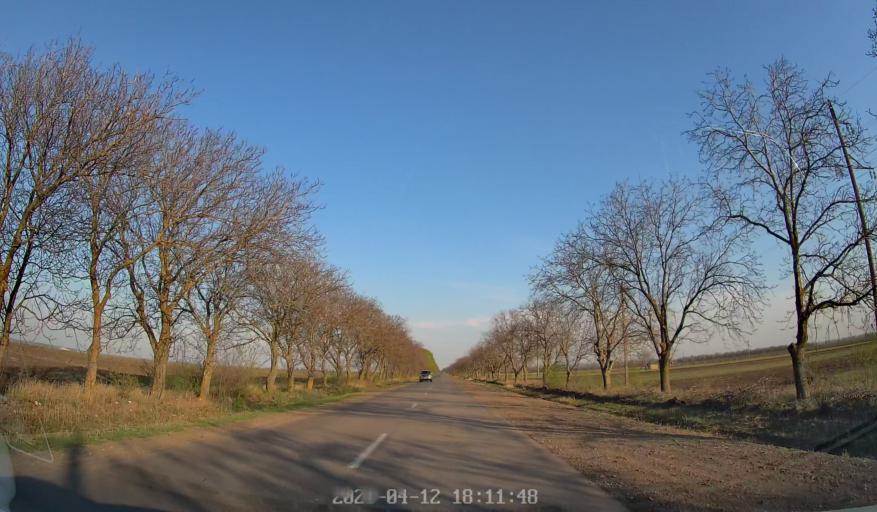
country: MD
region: Telenesti
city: Cocieri
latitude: 47.2824
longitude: 29.0925
